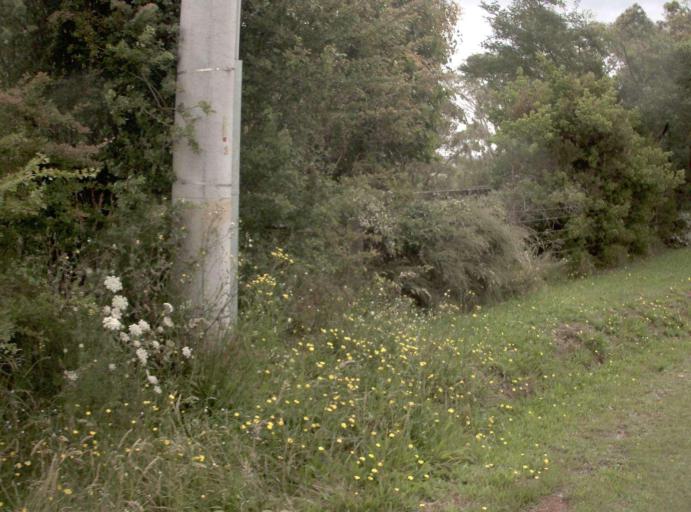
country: AU
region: Victoria
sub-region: Baw Baw
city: Warragul
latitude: -38.1399
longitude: 145.9861
